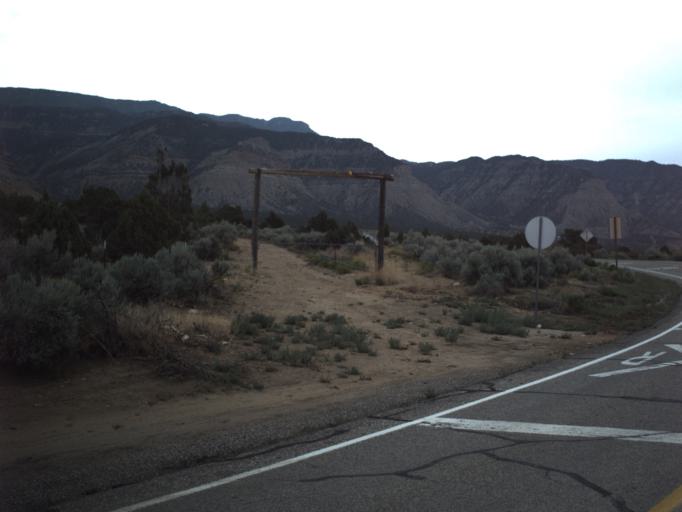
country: US
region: Utah
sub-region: Carbon County
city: East Carbon City
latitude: 39.5422
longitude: -110.4142
